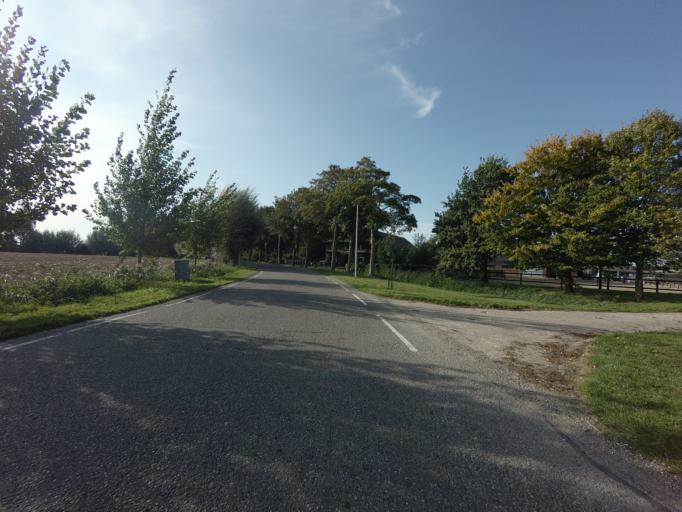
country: NL
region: Utrecht
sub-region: Gemeente Lopik
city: Lopik
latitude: 51.9410
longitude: 4.9668
